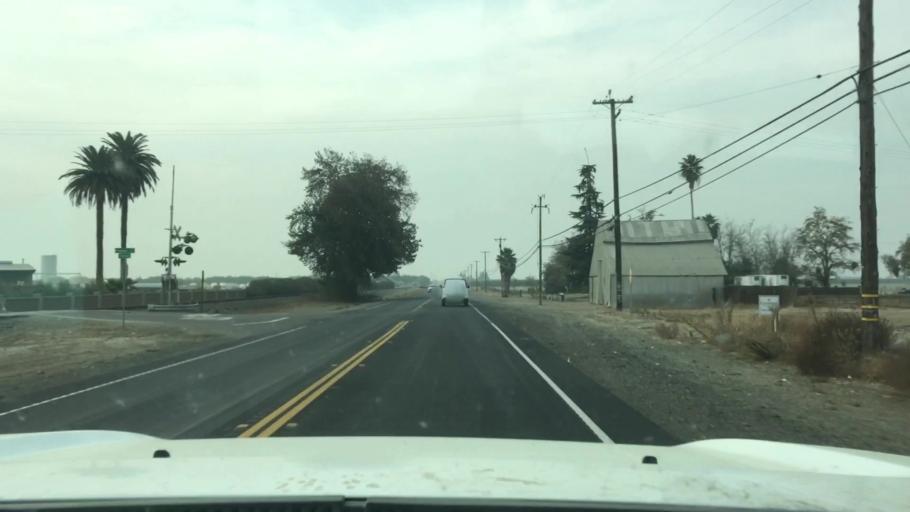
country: US
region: California
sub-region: San Joaquin County
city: Manteca
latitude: 37.8392
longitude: -121.1667
